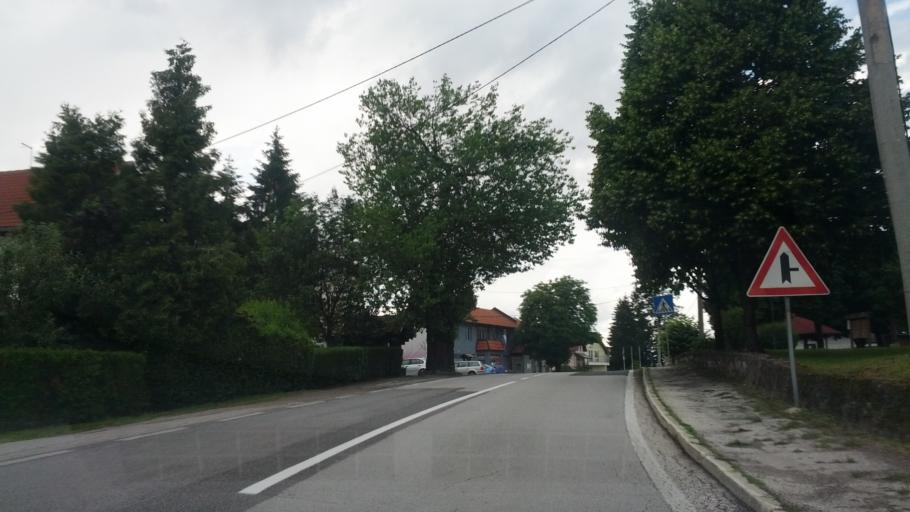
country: HR
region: Licko-Senjska
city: Jezerce
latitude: 44.9483
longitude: 15.6734
